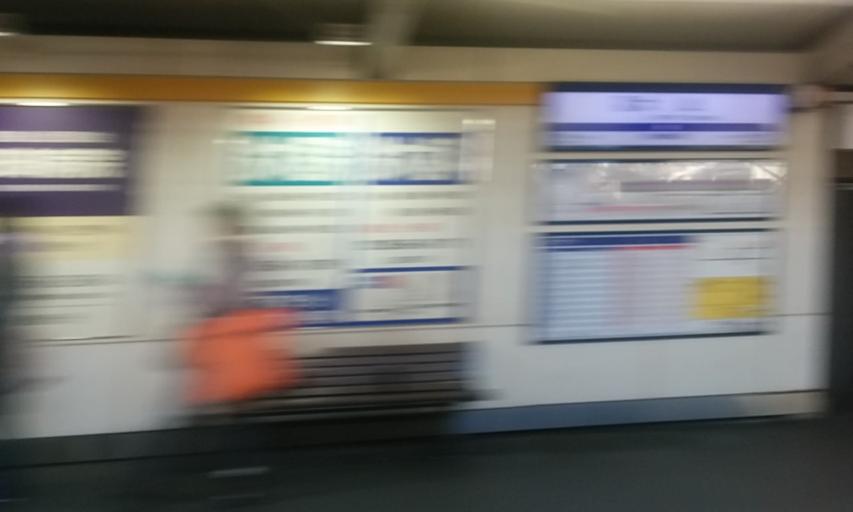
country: JP
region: Saitama
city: Kawaguchi
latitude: 35.7485
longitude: 139.7024
